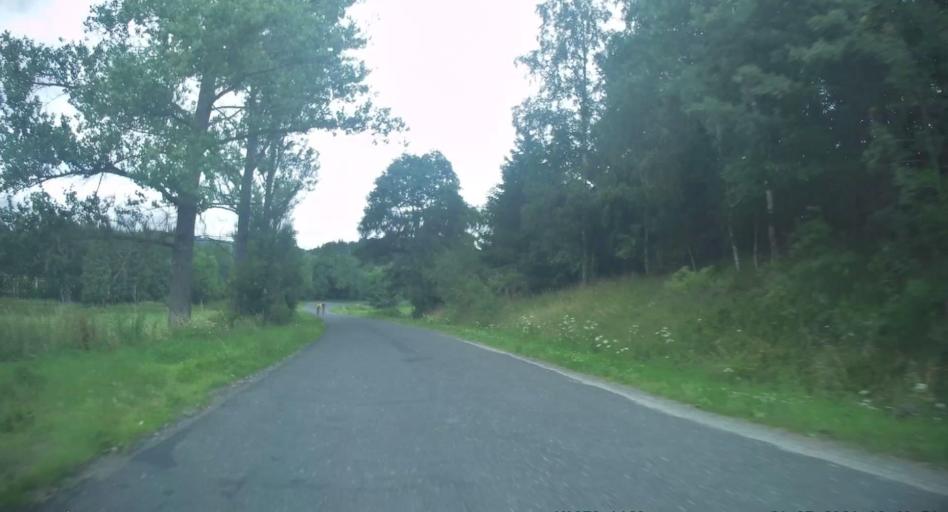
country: PL
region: Lower Silesian Voivodeship
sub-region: Powiat kamiennogorski
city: Marciszow
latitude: 50.8501
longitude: 15.9948
